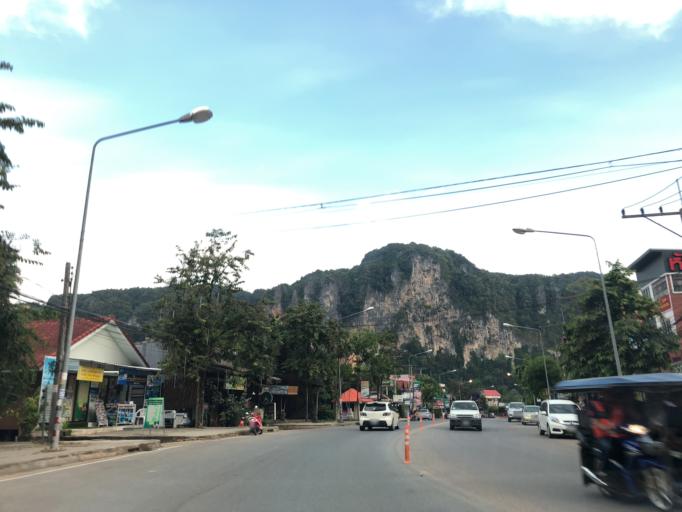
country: TH
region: Phangnga
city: Ban Ao Nang
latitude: 8.0379
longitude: 98.8335
